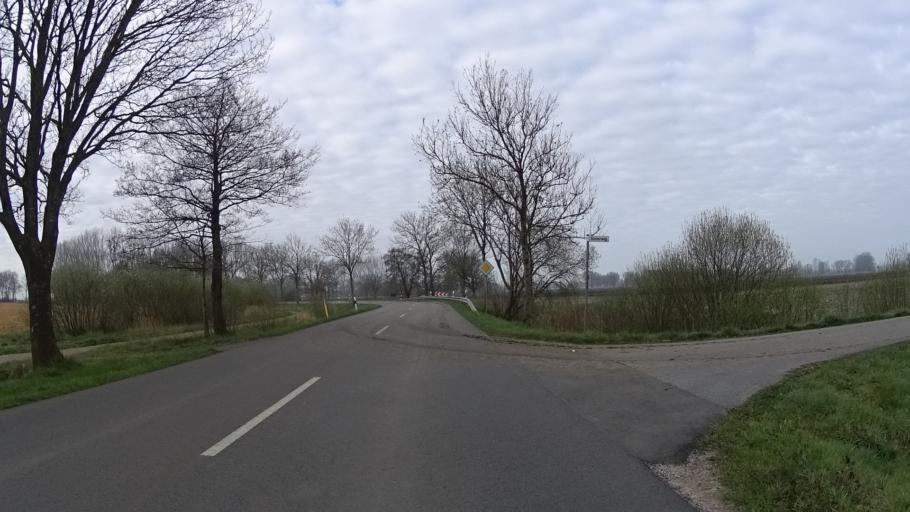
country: DE
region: Lower Saxony
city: Upgant-Schott
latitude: 53.4455
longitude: 7.3313
